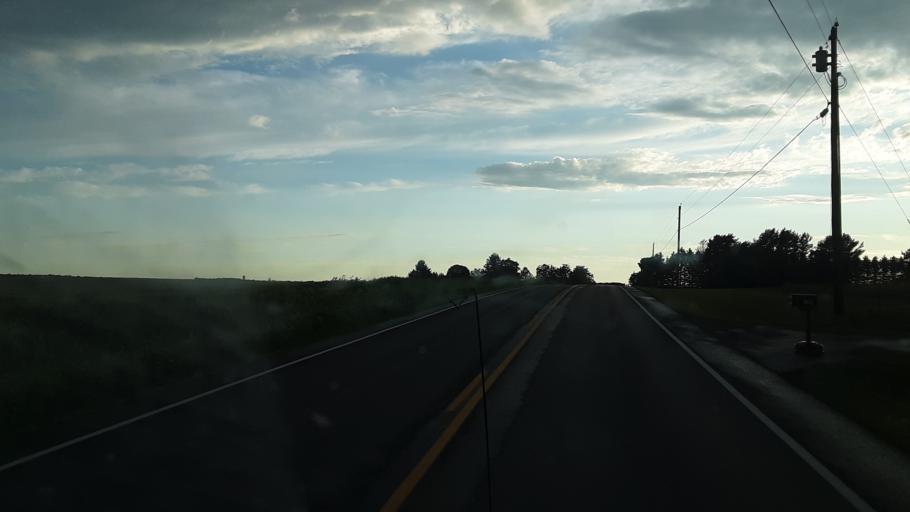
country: US
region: Maine
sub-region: Aroostook County
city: Easton
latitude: 46.6752
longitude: -67.9573
